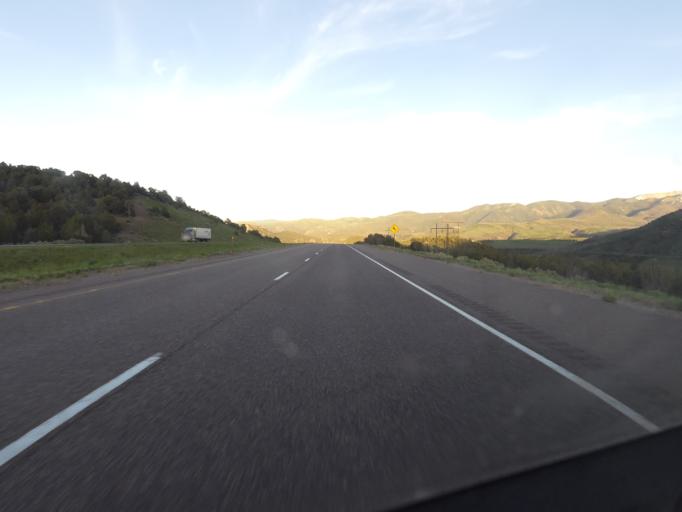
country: US
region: Utah
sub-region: Beaver County
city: Beaver
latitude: 38.5790
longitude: -112.4795
